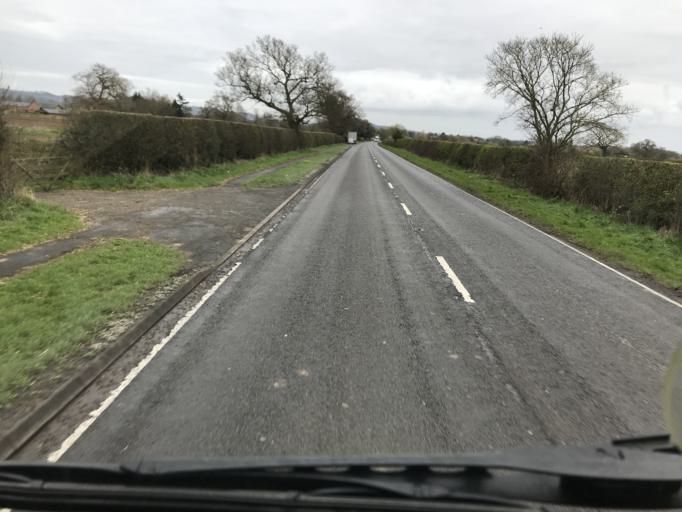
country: GB
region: England
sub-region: Cheshire West and Chester
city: Waverton
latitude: 53.1354
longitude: -2.8081
